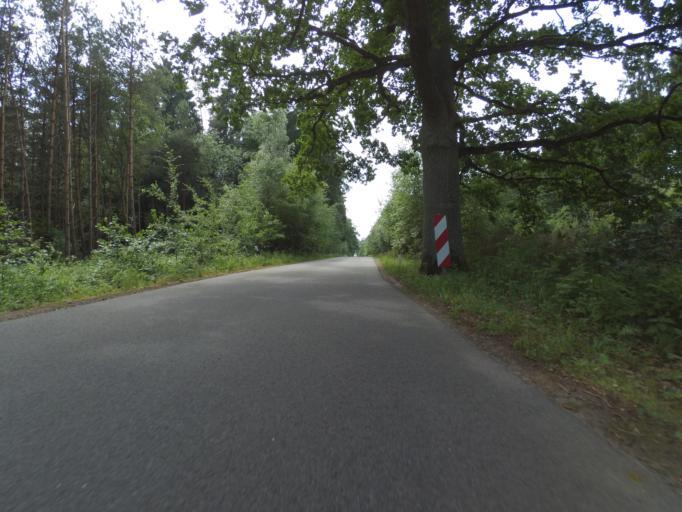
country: DE
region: Mecklenburg-Vorpommern
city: Malchow
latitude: 53.4433
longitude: 12.3539
